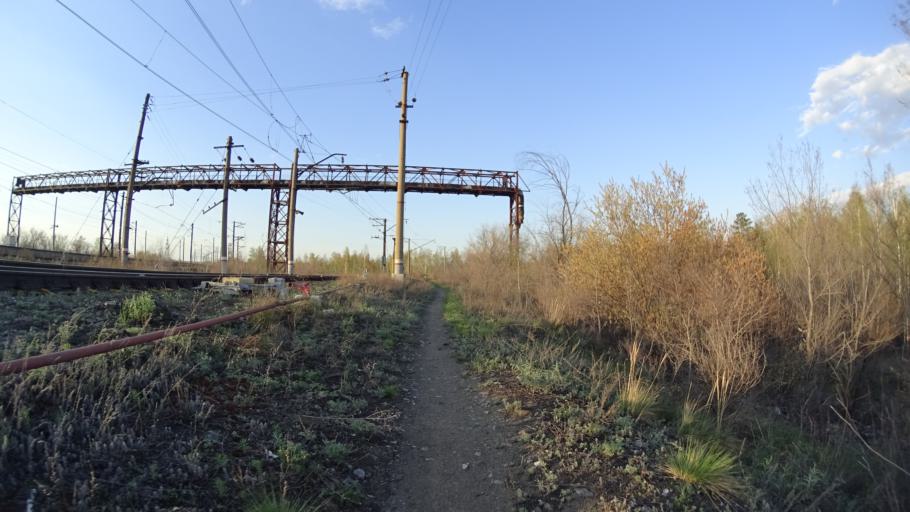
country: RU
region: Chelyabinsk
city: Troitsk
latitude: 54.0574
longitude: 61.6138
